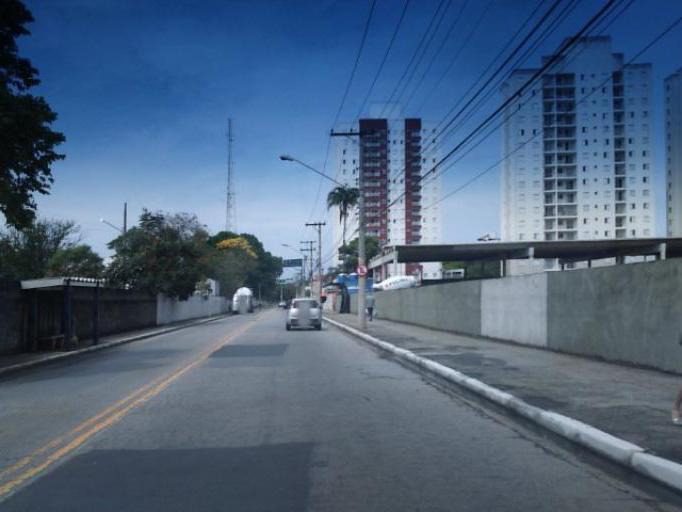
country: BR
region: Sao Paulo
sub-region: Sao Jose Dos Campos
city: Sao Jose dos Campos
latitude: -23.1948
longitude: -45.8761
